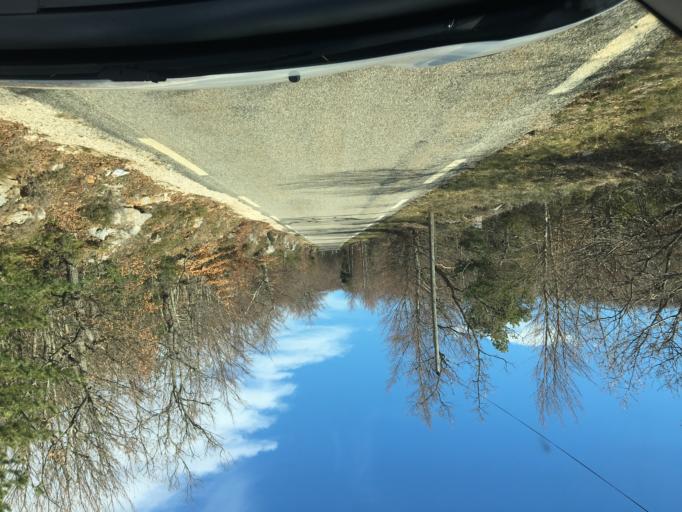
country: FR
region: Provence-Alpes-Cote d'Azur
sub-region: Departement du Vaucluse
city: Saint-Saturnin-les-Apt
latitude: 43.9740
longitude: 5.4617
